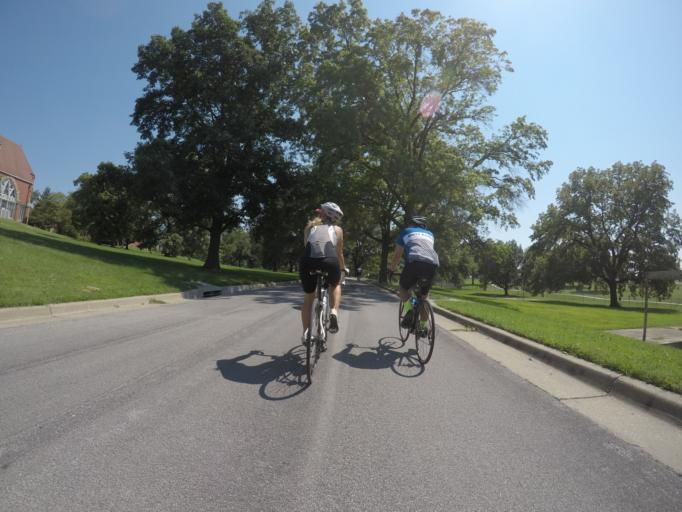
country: US
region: Kansas
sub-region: Leavenworth County
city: Lansing
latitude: 39.2769
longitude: -94.8972
